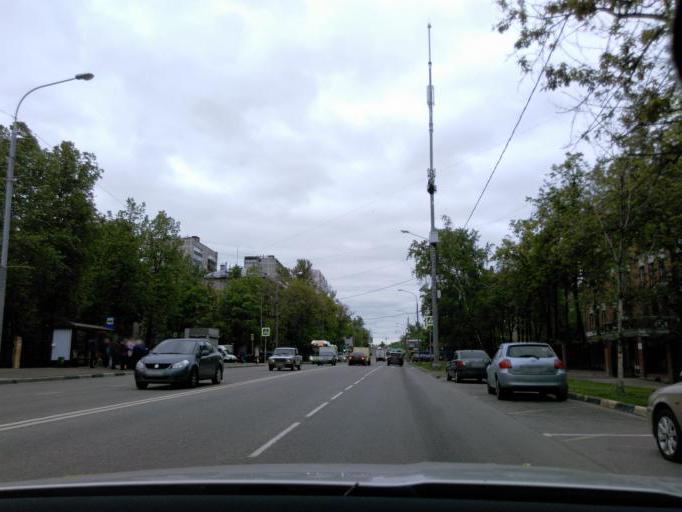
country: RU
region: Moscow
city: Zapadnoye Degunino
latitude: 55.8457
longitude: 37.5214
